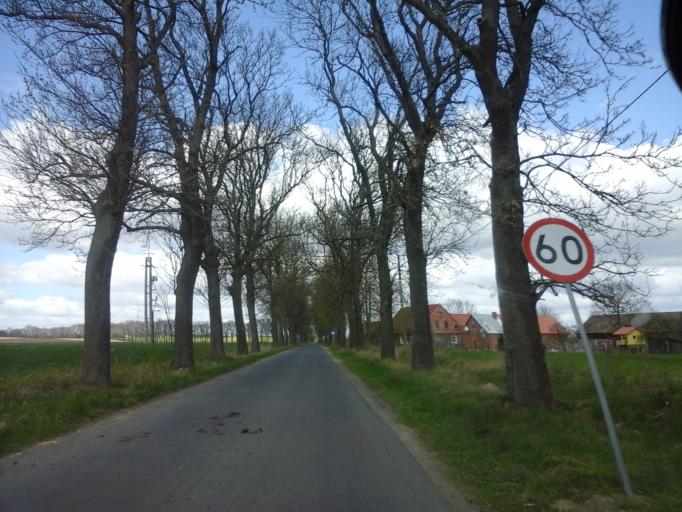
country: PL
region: West Pomeranian Voivodeship
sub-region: Powiat choszczenski
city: Recz
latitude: 53.1762
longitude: 15.6061
